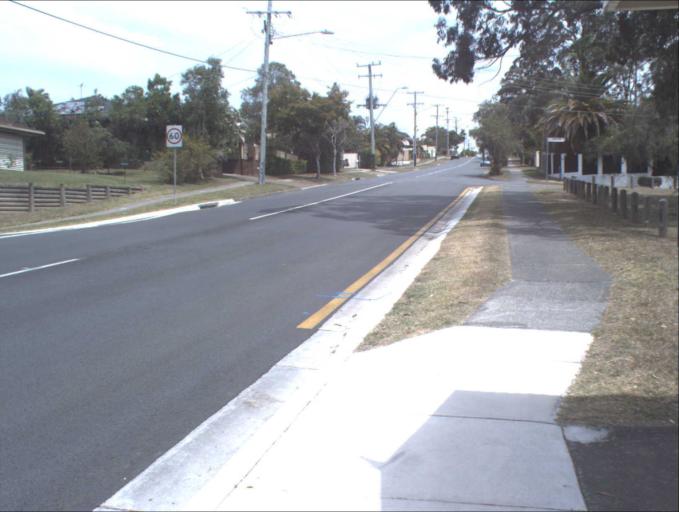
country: AU
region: Queensland
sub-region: Logan
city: Springwood
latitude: -27.6264
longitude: 153.1344
